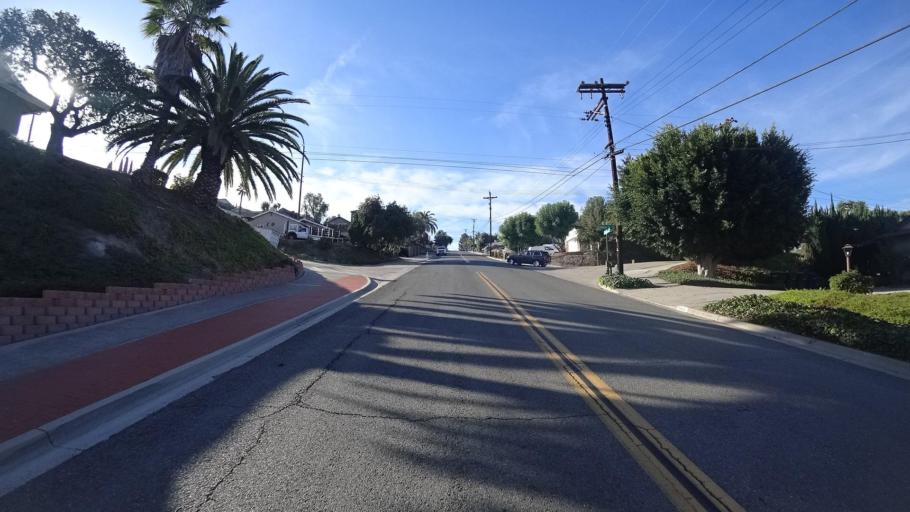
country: US
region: California
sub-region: San Diego County
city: Spring Valley
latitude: 32.7413
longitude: -116.9791
